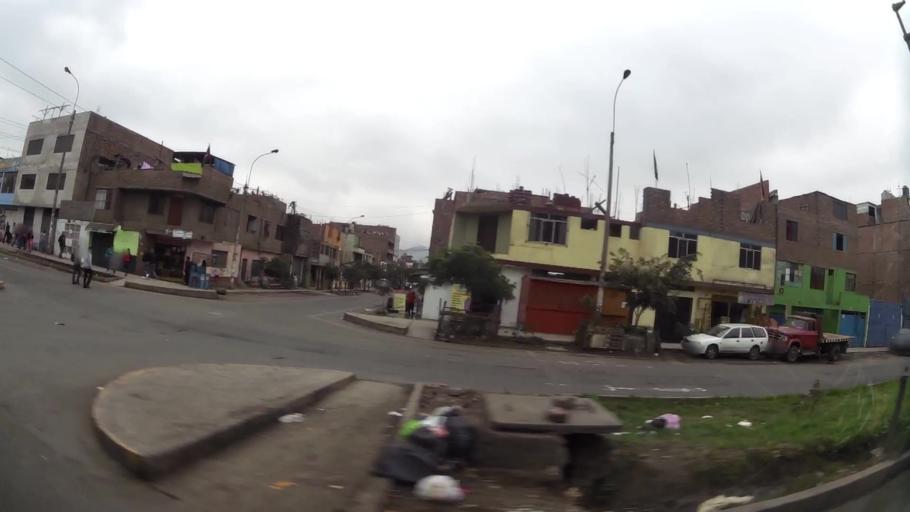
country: PE
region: Lima
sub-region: Lima
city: Vitarte
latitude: -12.0363
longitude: -76.9627
